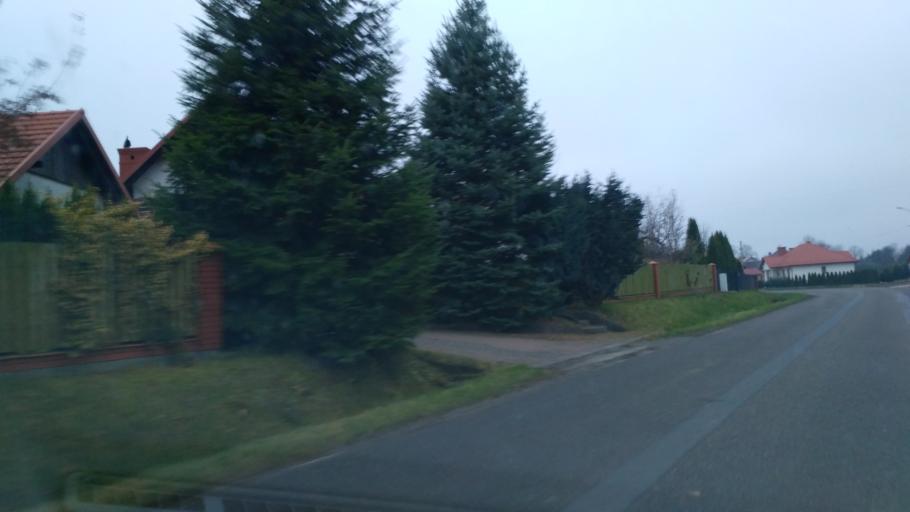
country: PL
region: Subcarpathian Voivodeship
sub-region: Powiat przeworski
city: Rozborz
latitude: 50.0615
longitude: 22.5237
